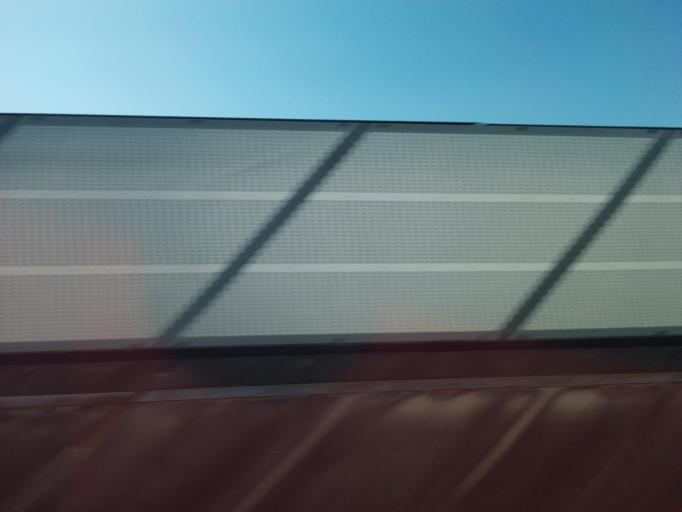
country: JP
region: Gifu
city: Ogaki
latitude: 35.3188
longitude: 136.6821
